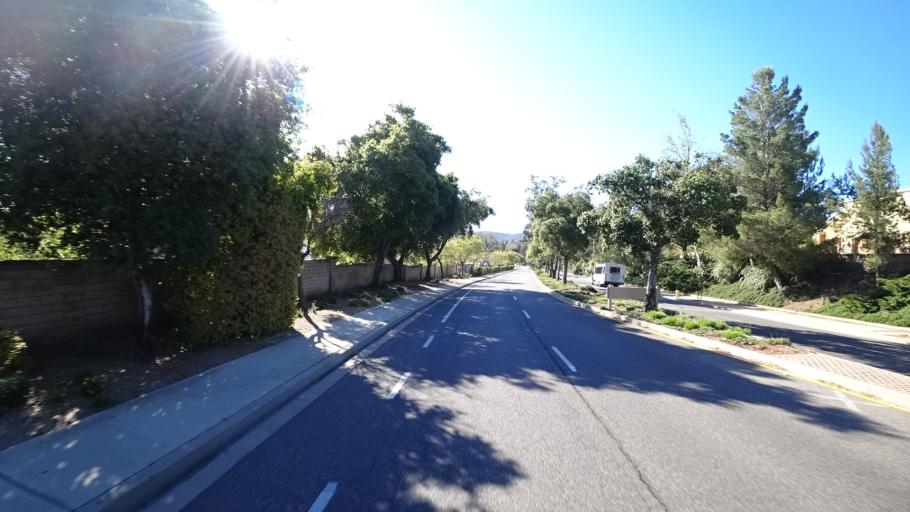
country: US
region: California
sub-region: Ventura County
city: Casa Conejo
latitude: 34.1872
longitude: -118.9088
